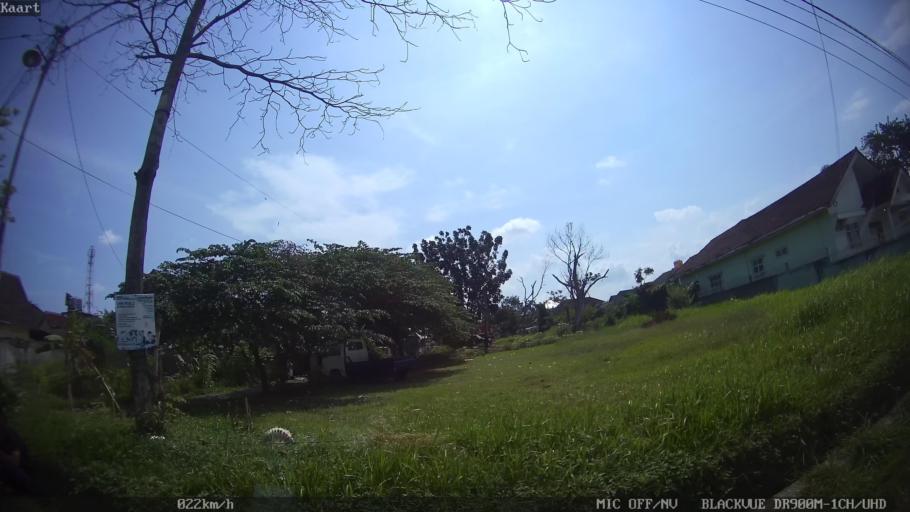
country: ID
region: Lampung
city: Kedaton
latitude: -5.3911
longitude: 105.2445
